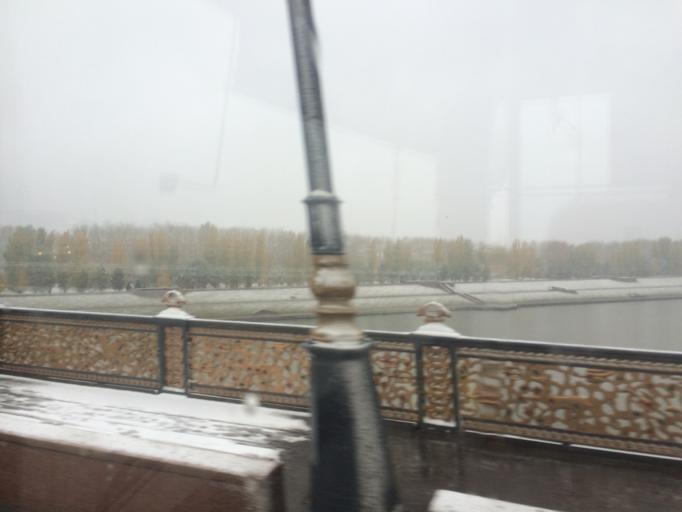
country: KZ
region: Astana Qalasy
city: Astana
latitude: 51.1388
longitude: 71.4439
